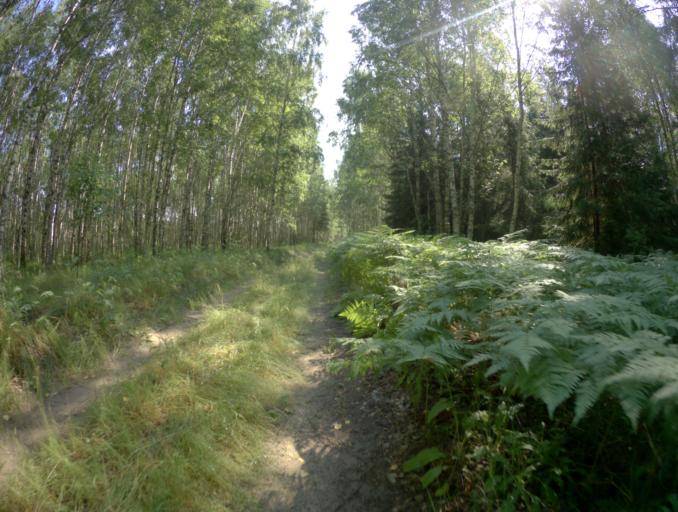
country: RU
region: Vladimir
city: Vyazniki
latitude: 56.3427
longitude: 42.1581
